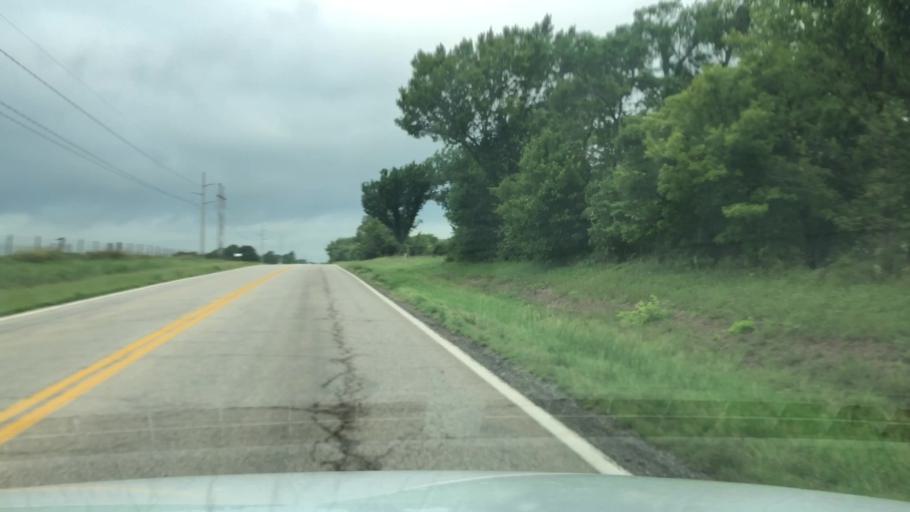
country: US
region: Oklahoma
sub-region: Nowata County
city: Nowata
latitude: 36.7136
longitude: -95.6674
